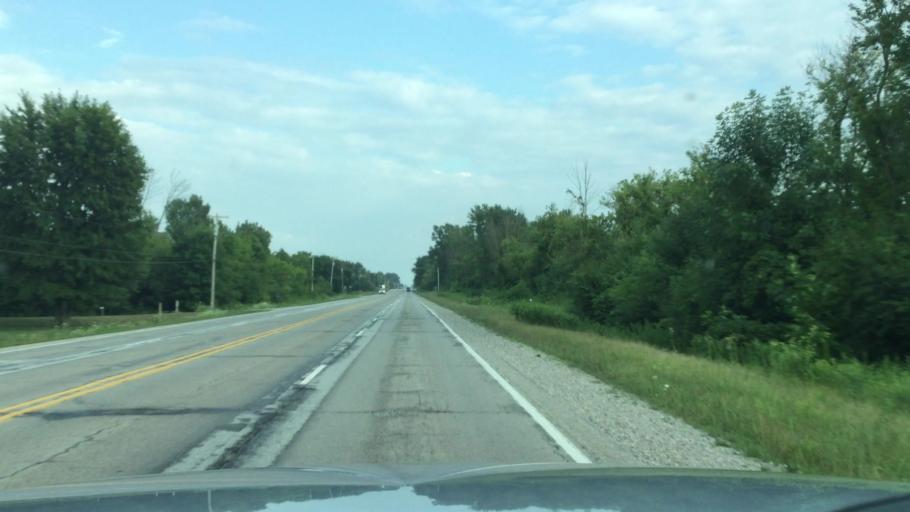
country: US
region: Michigan
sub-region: Saginaw County
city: Birch Run
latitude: 43.2740
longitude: -83.7874
